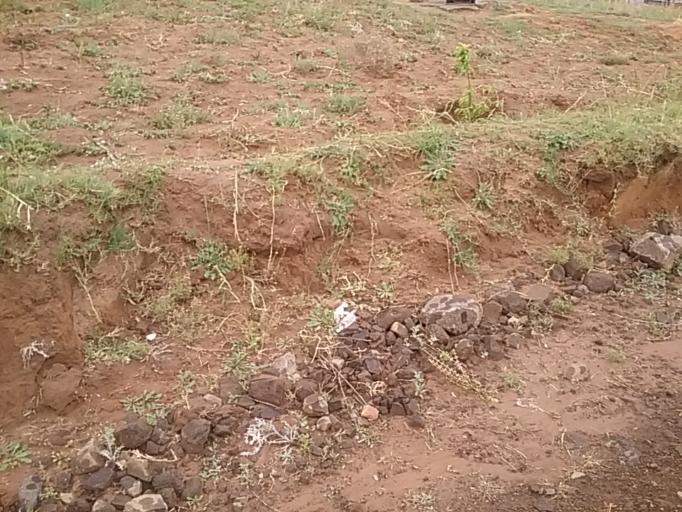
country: LS
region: Berea
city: Teyateyaneng
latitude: -29.1350
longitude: 27.7393
